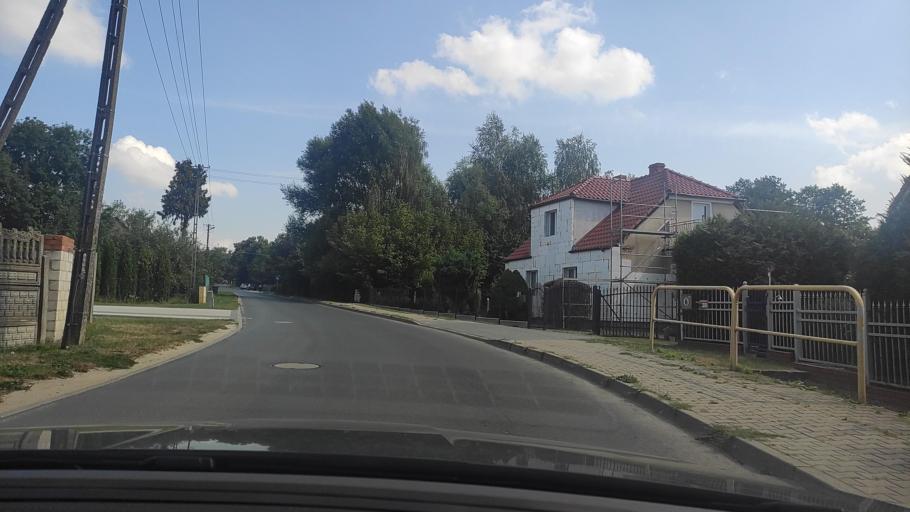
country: PL
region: Greater Poland Voivodeship
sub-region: Powiat poznanski
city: Kostrzyn
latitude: 52.4780
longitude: 17.1856
